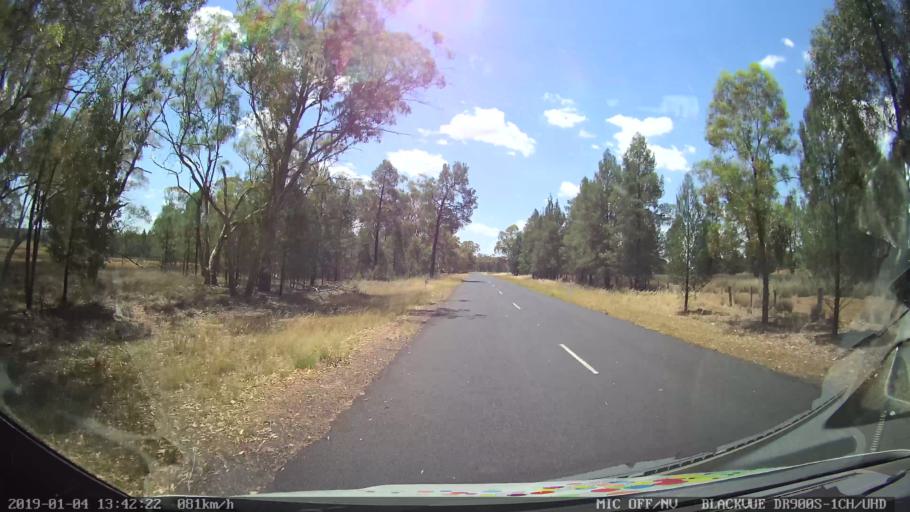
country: AU
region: New South Wales
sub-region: Dubbo Municipality
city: Dubbo
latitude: -32.4905
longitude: 148.5551
